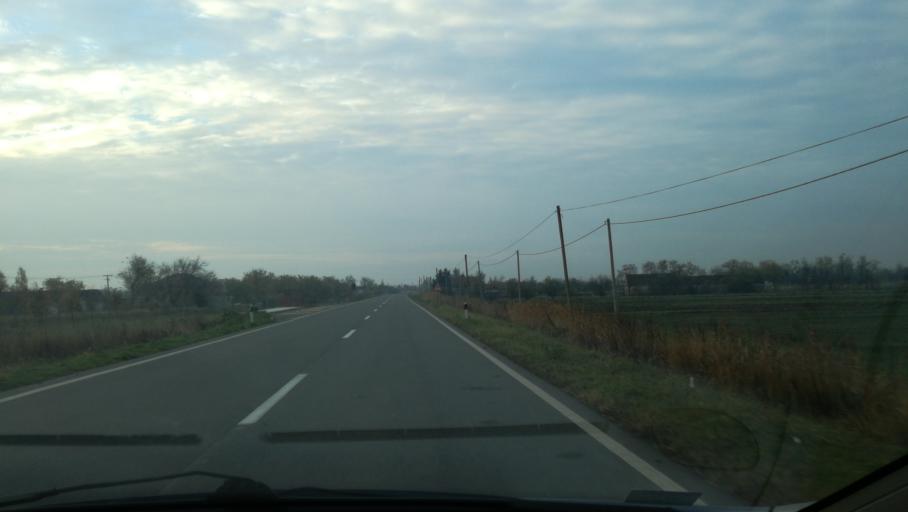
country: RS
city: Banatska Topola
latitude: 45.6884
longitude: 20.4229
